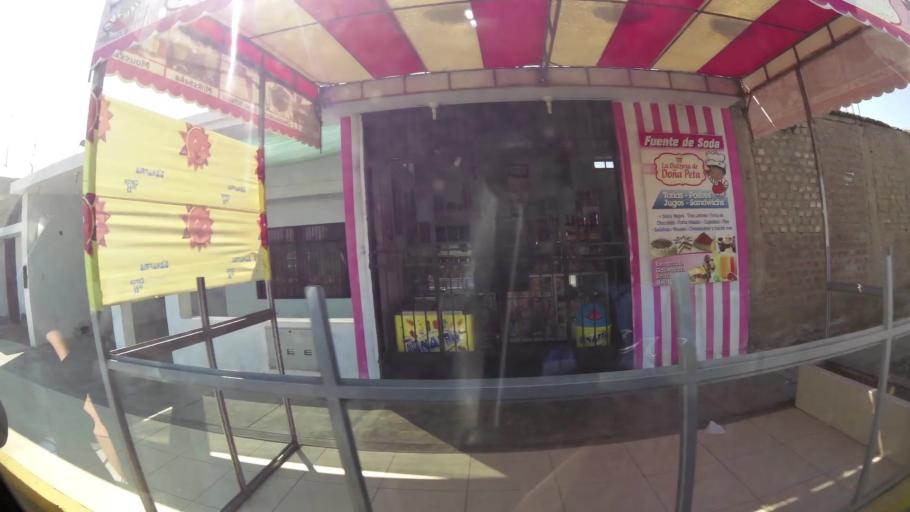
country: PE
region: Ica
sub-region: Provincia de Ica
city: La Tinguina
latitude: -14.0314
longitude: -75.7037
